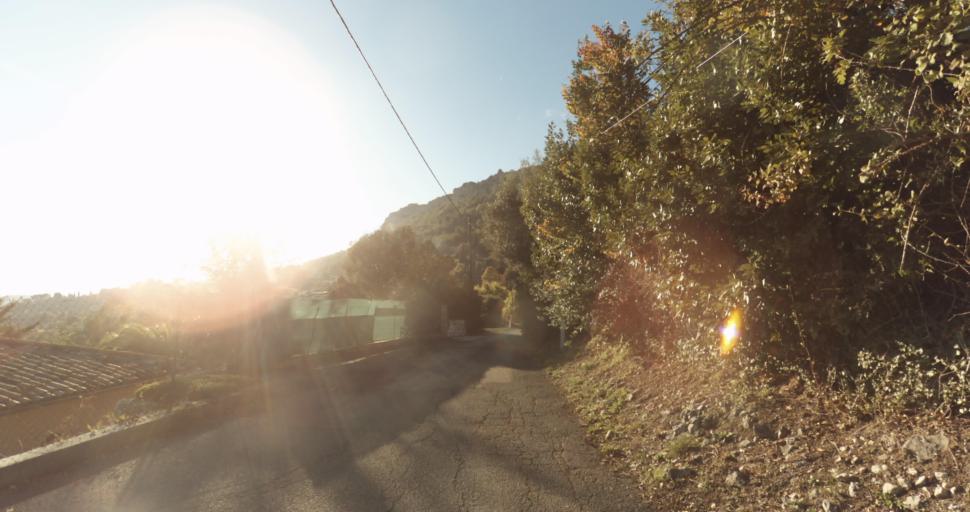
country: FR
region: Provence-Alpes-Cote d'Azur
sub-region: Departement des Alpes-Maritimes
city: Vence
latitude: 43.7389
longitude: 7.1241
